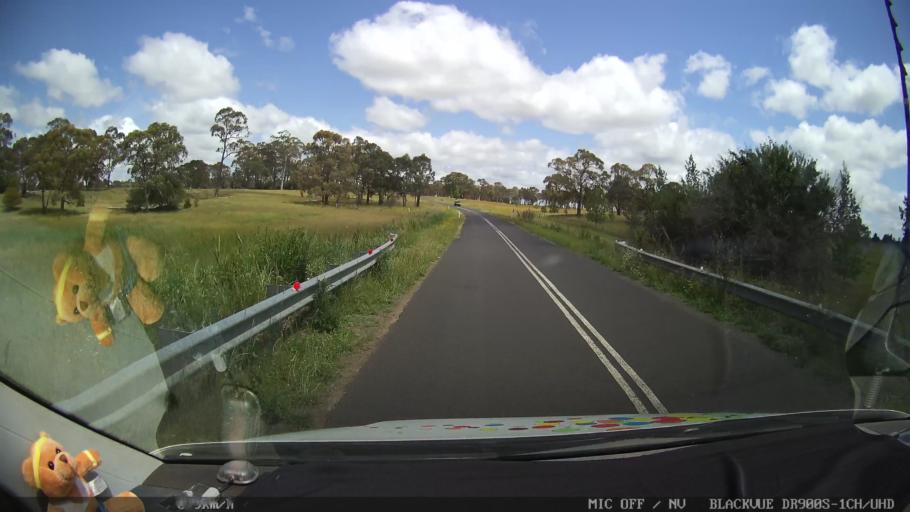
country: AU
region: New South Wales
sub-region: Glen Innes Severn
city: Glen Innes
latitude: -29.6392
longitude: 151.6866
